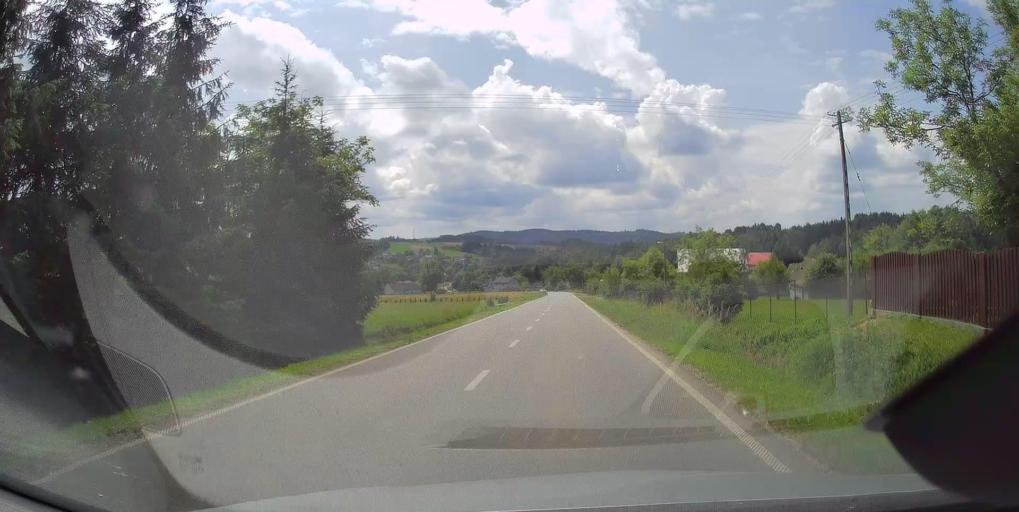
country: PL
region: Lesser Poland Voivodeship
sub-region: Powiat nowosadecki
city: Korzenna
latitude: 49.6808
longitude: 20.7759
